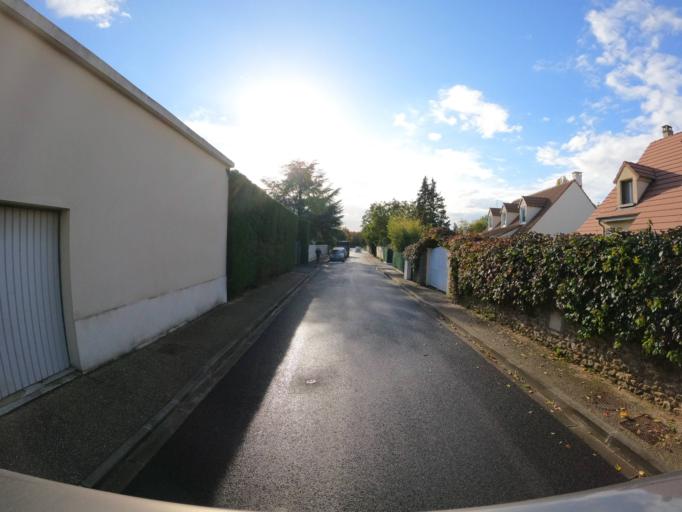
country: FR
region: Ile-de-France
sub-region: Departement de Seine-et-Marne
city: Bailly-Romainvilliers
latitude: 48.8463
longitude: 2.8224
